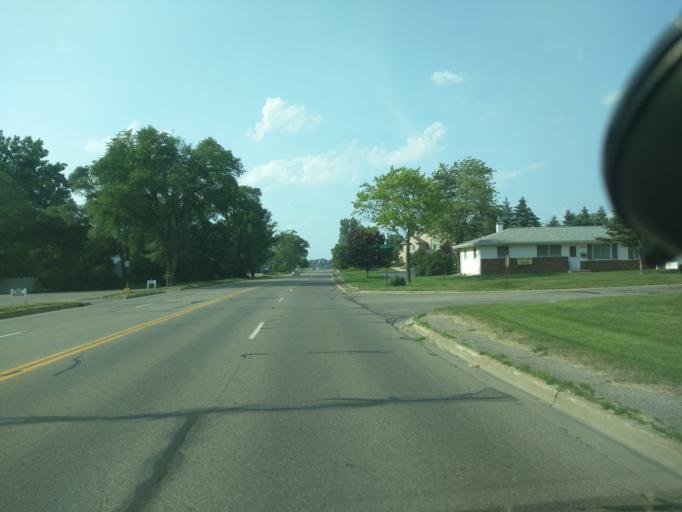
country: US
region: Michigan
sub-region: Jackson County
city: Jackson
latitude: 42.2565
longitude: -84.4477
